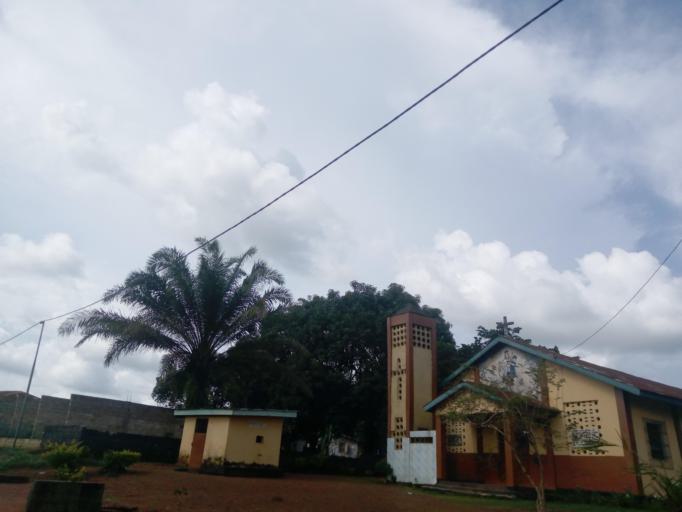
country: SL
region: Northern Province
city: Makeni
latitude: 8.9193
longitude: -12.0302
